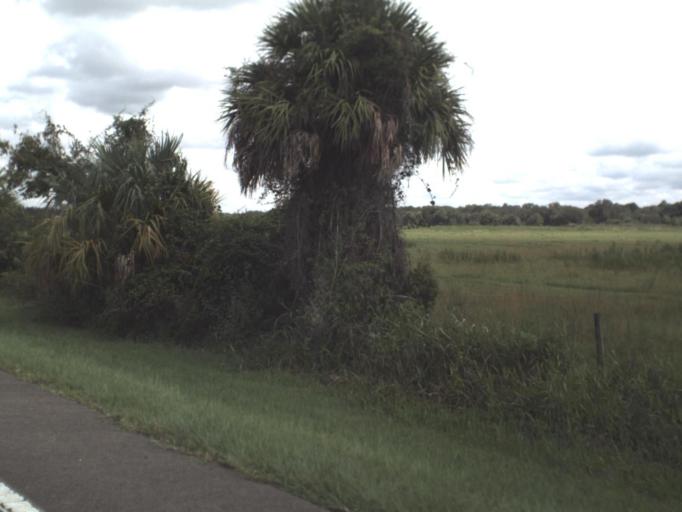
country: US
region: Florida
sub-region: DeSoto County
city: Nocatee
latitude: 27.1973
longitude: -82.0799
